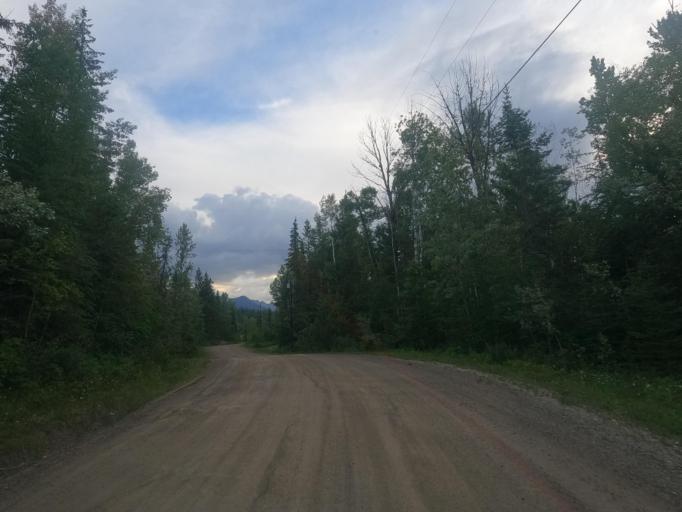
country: CA
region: British Columbia
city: Golden
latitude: 51.4474
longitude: -117.0070
